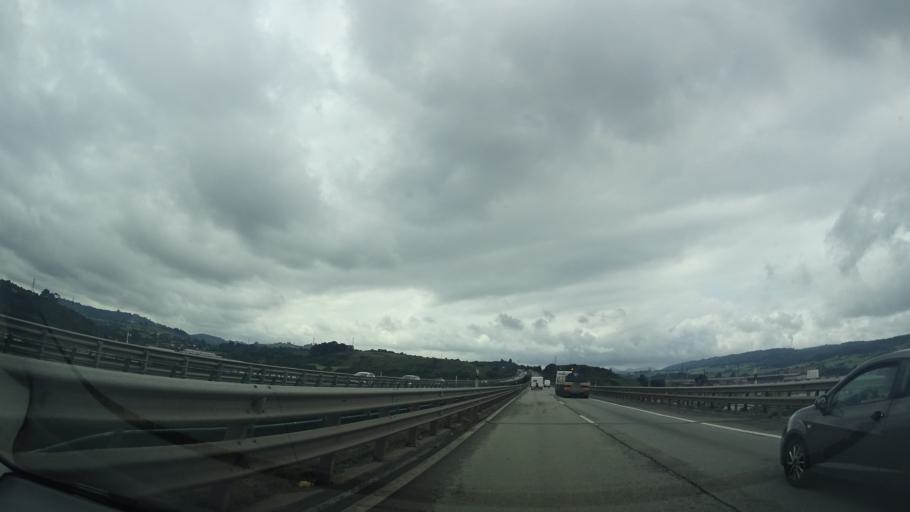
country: ES
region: Asturias
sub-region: Province of Asturias
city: Natahoyo
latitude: 43.5179
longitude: -5.7216
